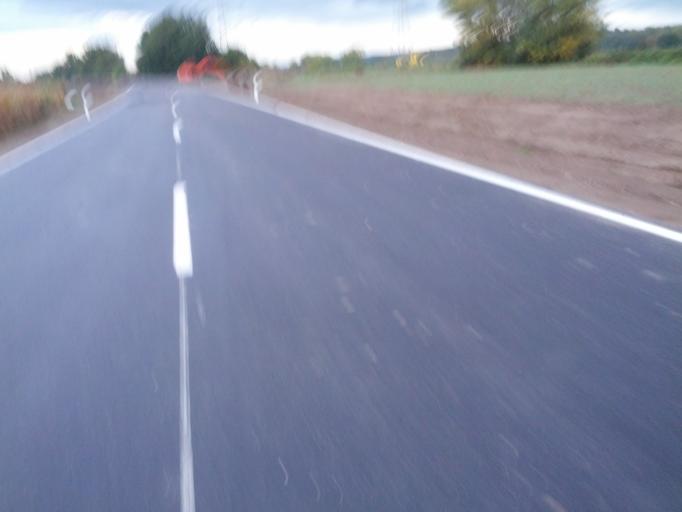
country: DE
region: Baden-Wuerttemberg
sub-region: Freiburg Region
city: Eichstetten
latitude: 48.0779
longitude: 7.7524
